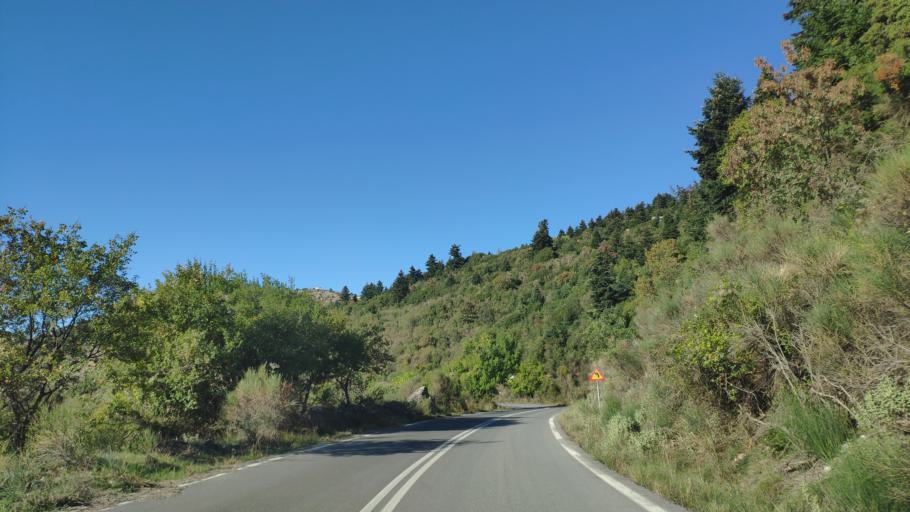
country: GR
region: Peloponnese
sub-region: Nomos Arkadias
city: Dimitsana
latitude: 37.5741
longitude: 22.0620
